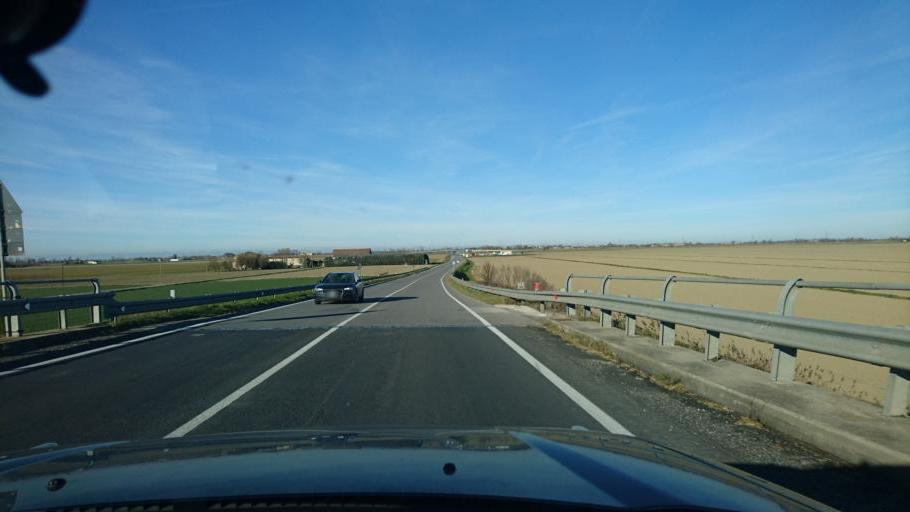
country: IT
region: Veneto
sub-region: Provincia di Rovigo
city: Bottrighe
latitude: 45.0282
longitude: 12.0989
